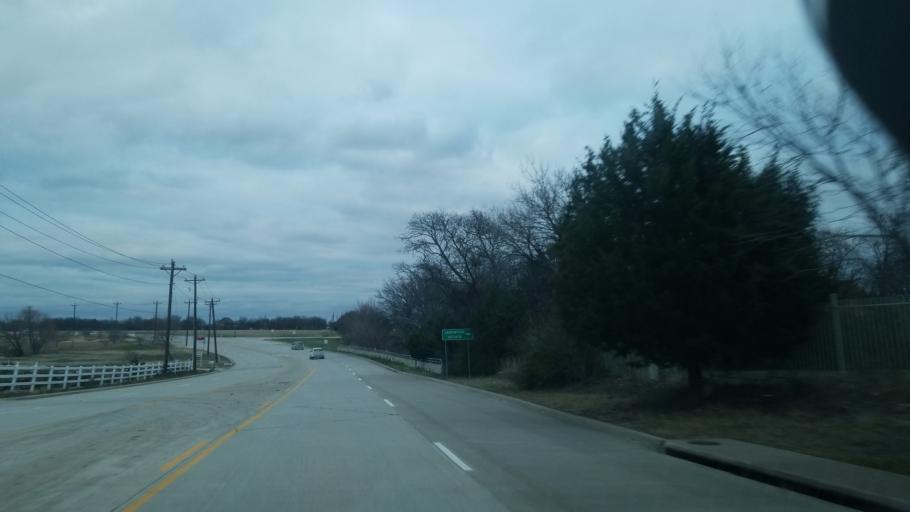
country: US
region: Texas
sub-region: Denton County
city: Little Elm
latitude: 33.1439
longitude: -96.9784
